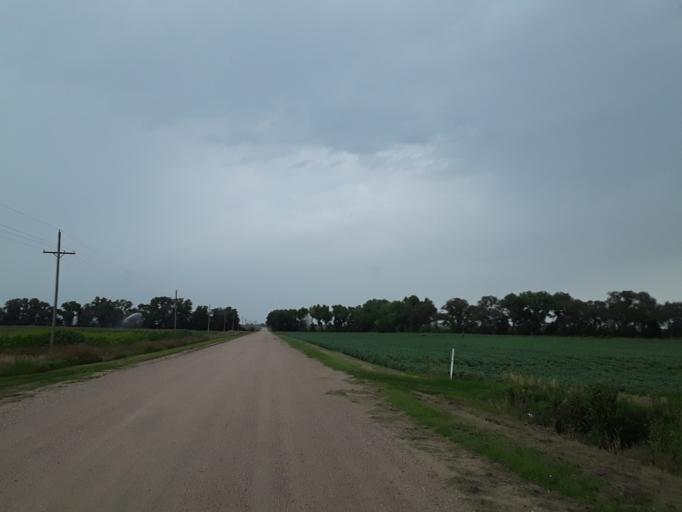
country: US
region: Nebraska
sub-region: Saunders County
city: Yutan
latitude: 41.1626
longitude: -96.4448
